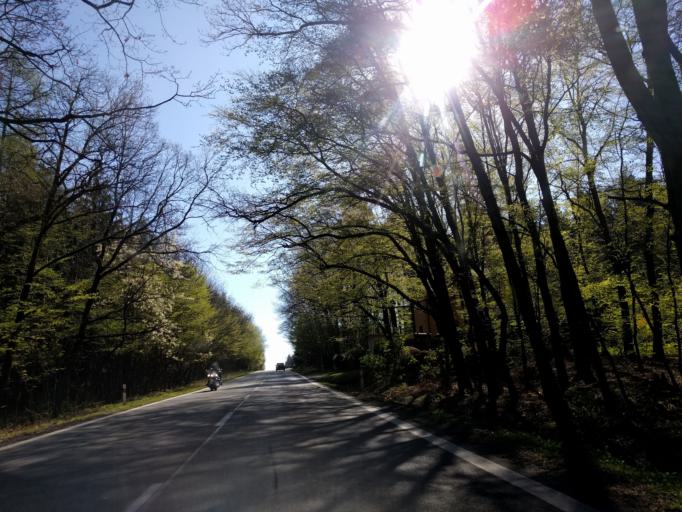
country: CZ
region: Central Bohemia
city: Mukarov
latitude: 49.9877
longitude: 14.7768
